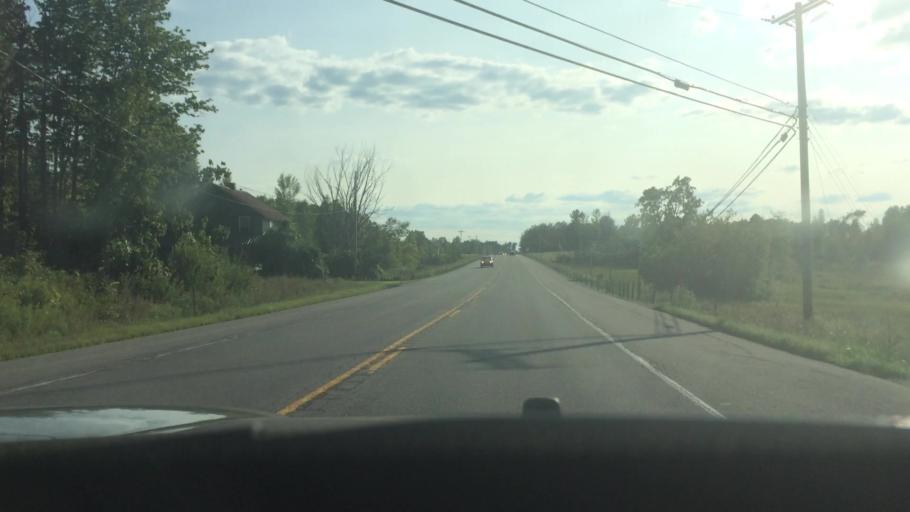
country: US
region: New York
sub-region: St. Lawrence County
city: Potsdam
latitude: 44.6448
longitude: -75.0582
